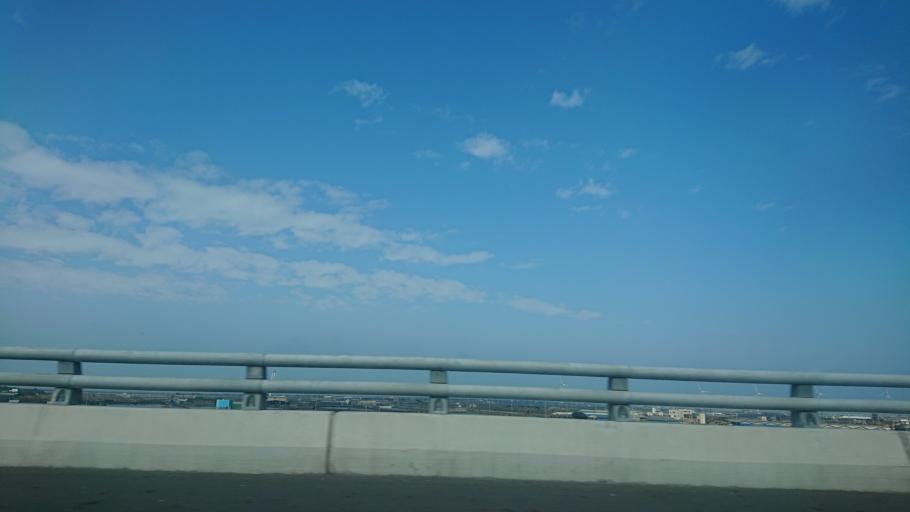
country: TW
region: Taiwan
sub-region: Changhua
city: Chang-hua
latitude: 23.9684
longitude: 120.3402
